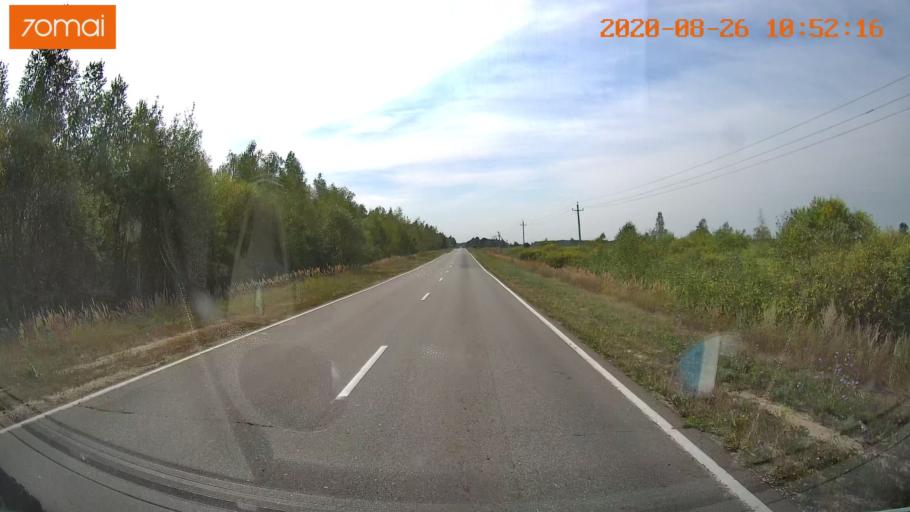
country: RU
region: Rjazan
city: Lashma
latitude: 54.6594
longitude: 41.1537
